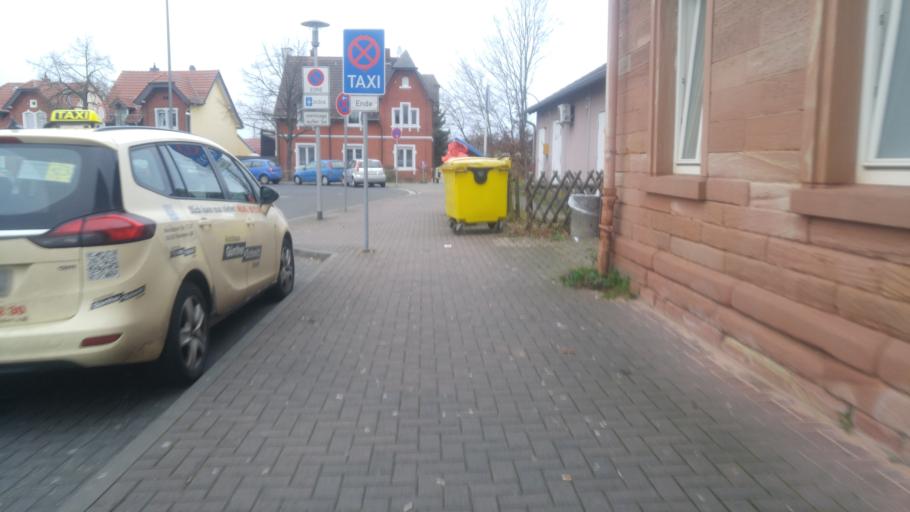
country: DE
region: Hesse
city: Raunheim
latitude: 50.0102
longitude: 8.4551
